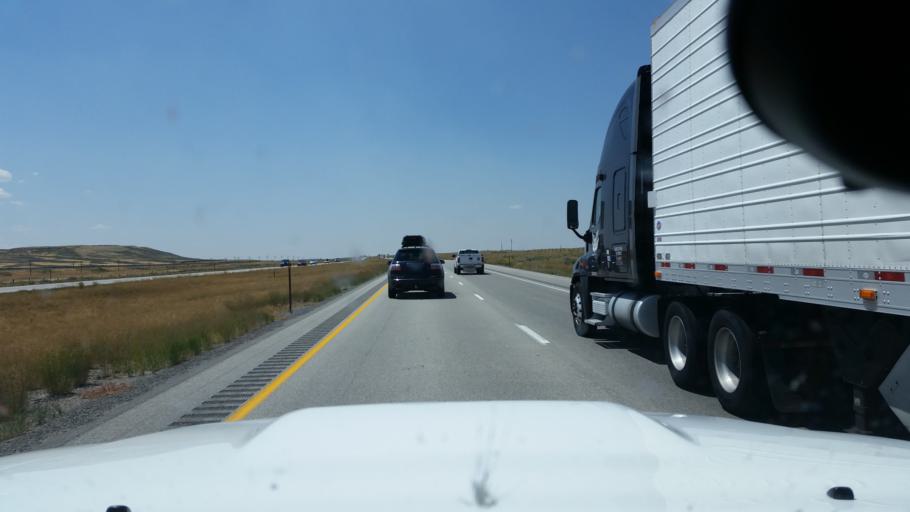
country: US
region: Wyoming
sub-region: Sweetwater County
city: Rock Springs
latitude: 41.6381
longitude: -108.2340
